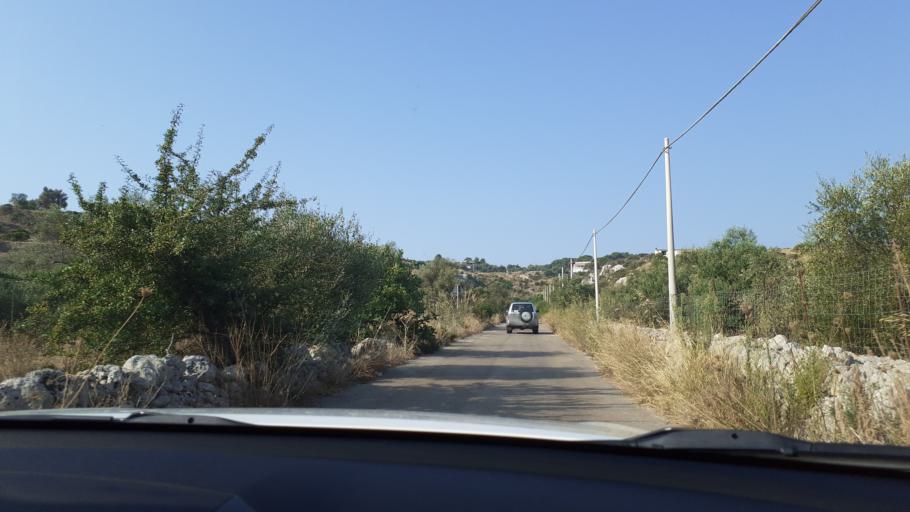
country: IT
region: Sicily
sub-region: Provincia di Siracusa
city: Cassibile
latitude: 36.9814
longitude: 15.1625
